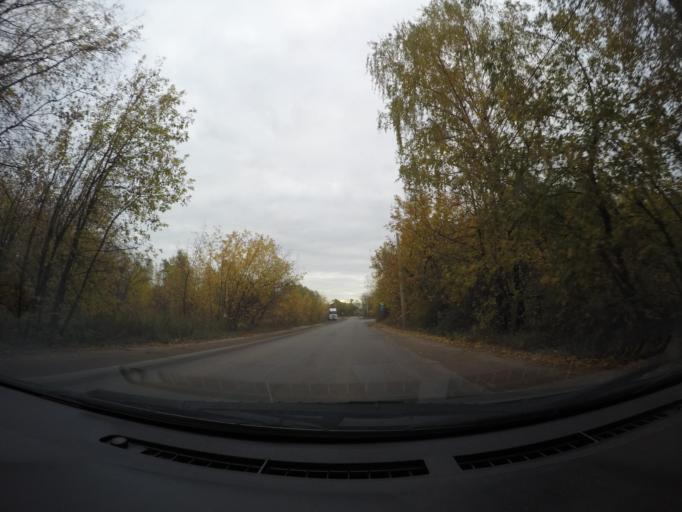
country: RU
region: Moskovskaya
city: Staraya Kupavna
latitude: 55.7964
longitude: 38.1808
